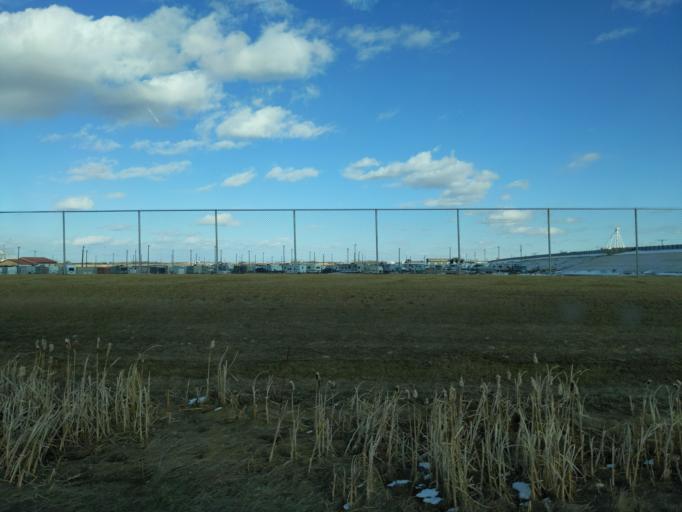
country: CA
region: Saskatchewan
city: Lloydminster
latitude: 53.2463
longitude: -109.9791
